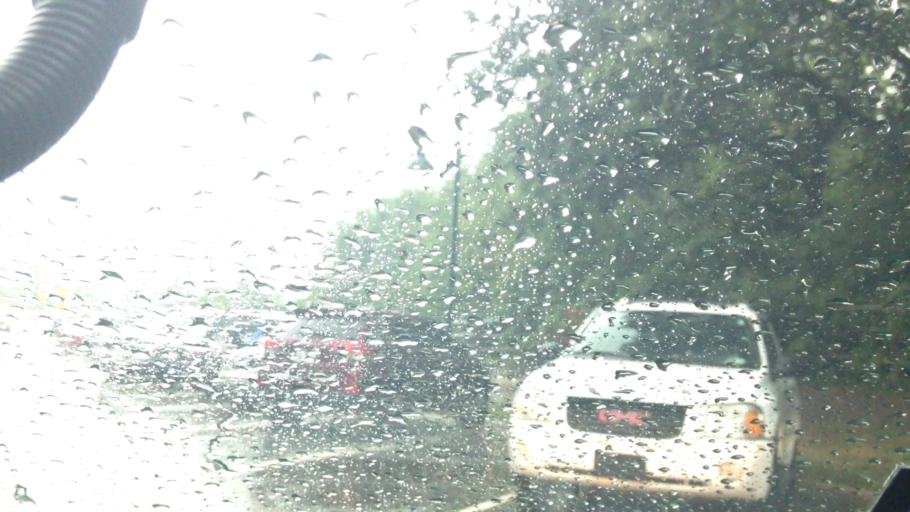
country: US
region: Kansas
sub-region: Johnson County
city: Leawood
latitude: 38.9357
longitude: -94.6316
